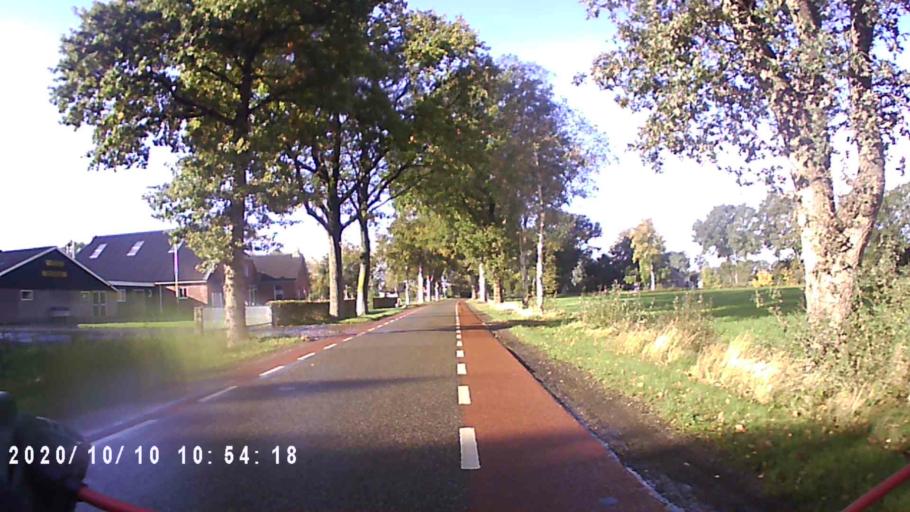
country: NL
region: Friesland
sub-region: Gemeente Achtkarspelen
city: Surhuisterveen
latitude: 53.1550
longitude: 6.2134
